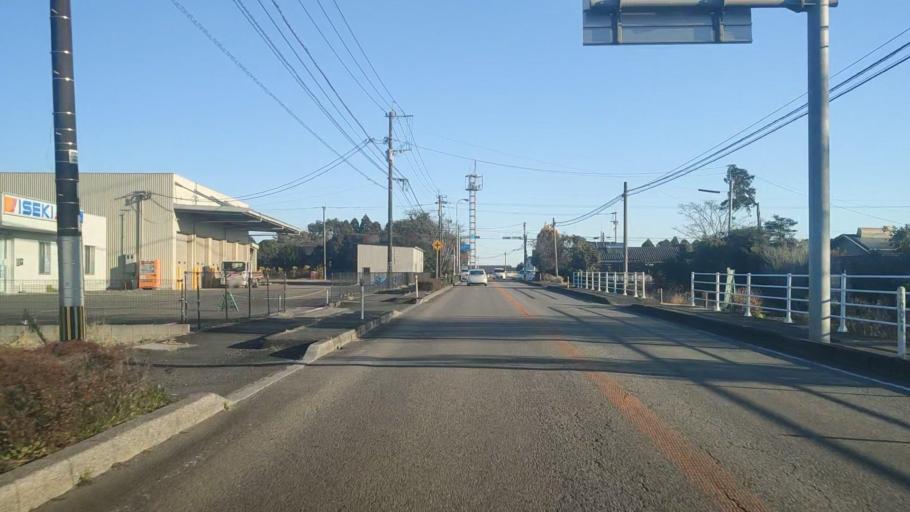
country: JP
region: Miyazaki
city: Takanabe
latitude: 32.1765
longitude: 131.5208
